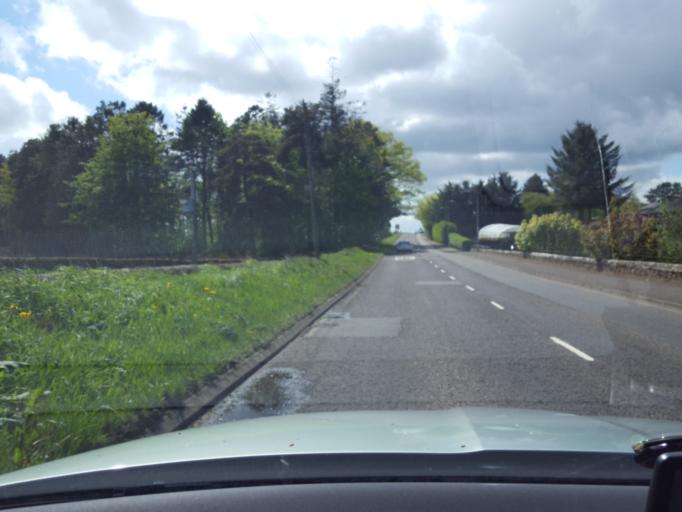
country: GB
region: Scotland
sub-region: Angus
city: Brechin
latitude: 56.7527
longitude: -2.6445
